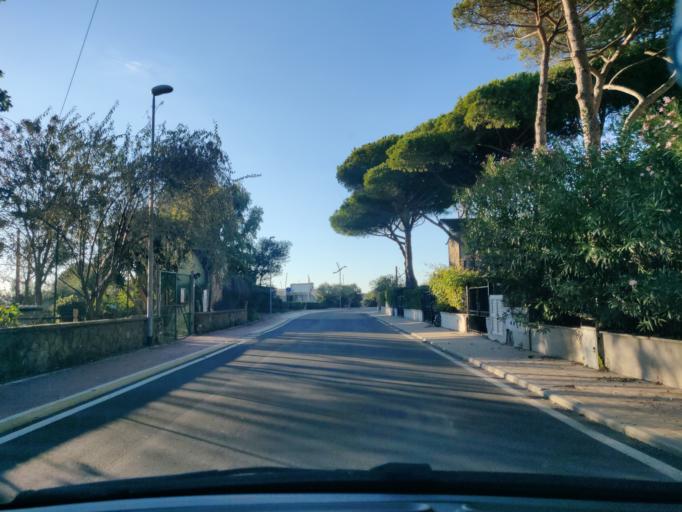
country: IT
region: Latium
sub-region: Provincia di Viterbo
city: Tarquinia
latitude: 42.2167
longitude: 11.7099
